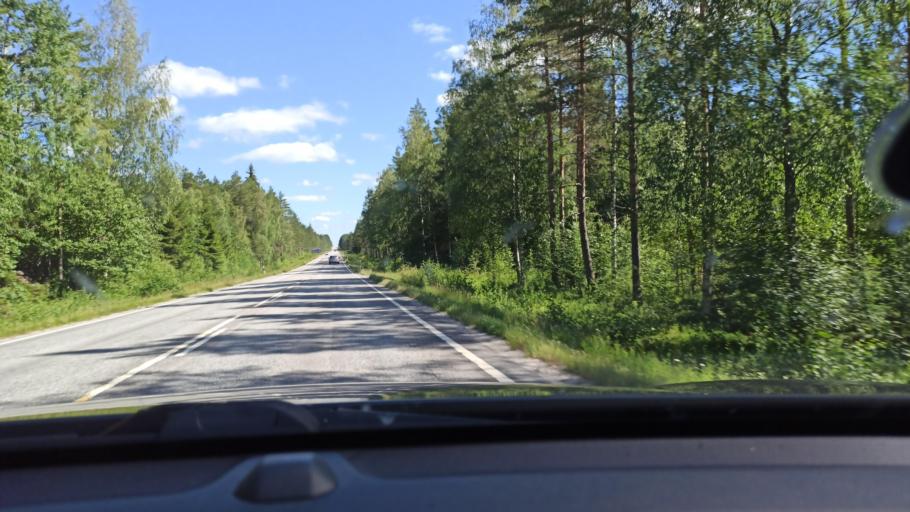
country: FI
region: Ostrobothnia
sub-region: Vaasa
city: Malax
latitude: 62.9751
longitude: 21.6036
